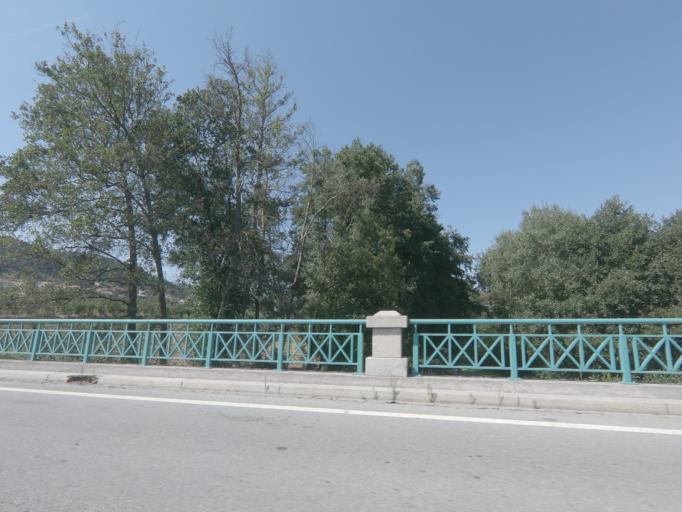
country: PT
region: Viseu
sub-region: Tarouca
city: Tarouca
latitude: 41.0286
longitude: -7.7566
